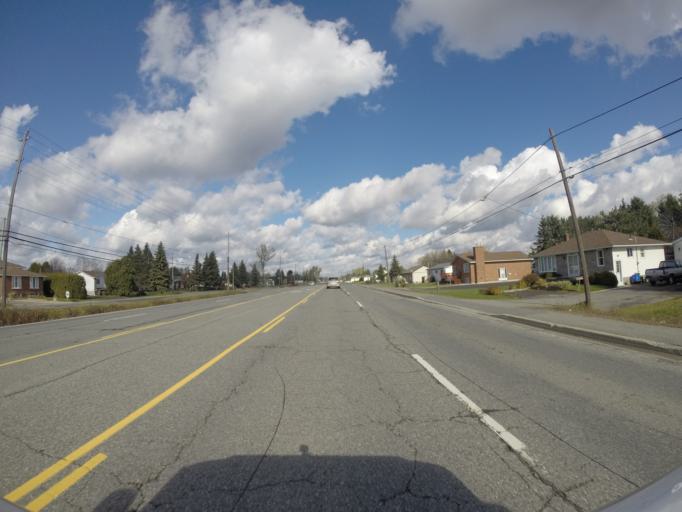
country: CA
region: Ontario
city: Greater Sudbury
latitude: 46.6329
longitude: -81.0080
